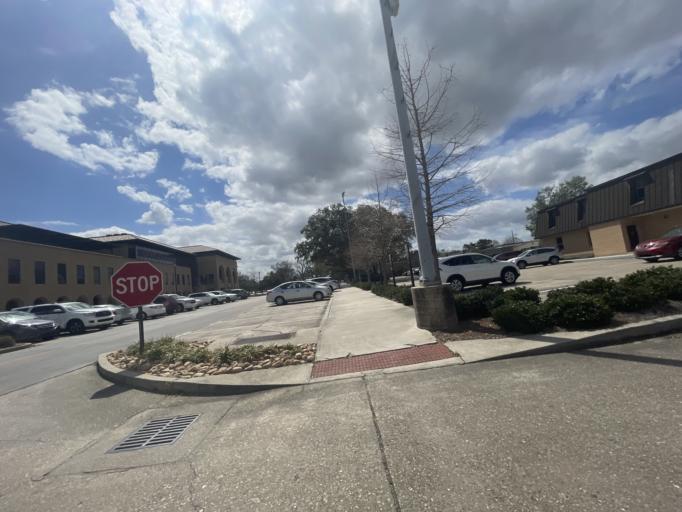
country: US
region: Louisiana
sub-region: East Baton Rouge Parish
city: Baton Rouge
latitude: 30.4087
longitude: -91.1806
